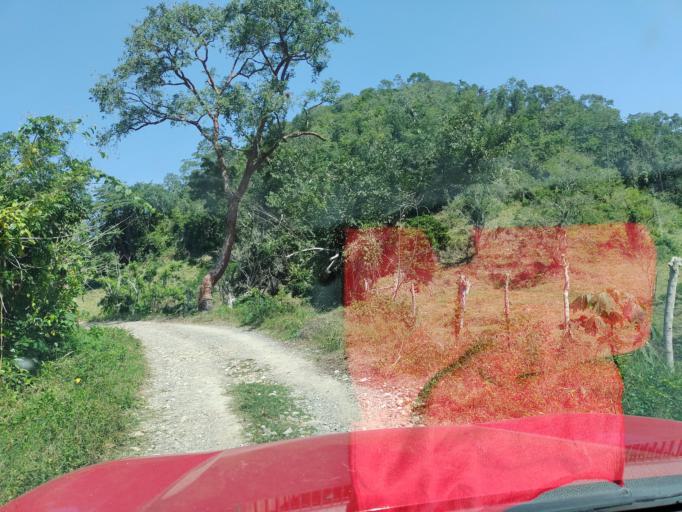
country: MX
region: Veracruz
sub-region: Papantla
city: Polutla
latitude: 20.5049
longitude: -97.2129
